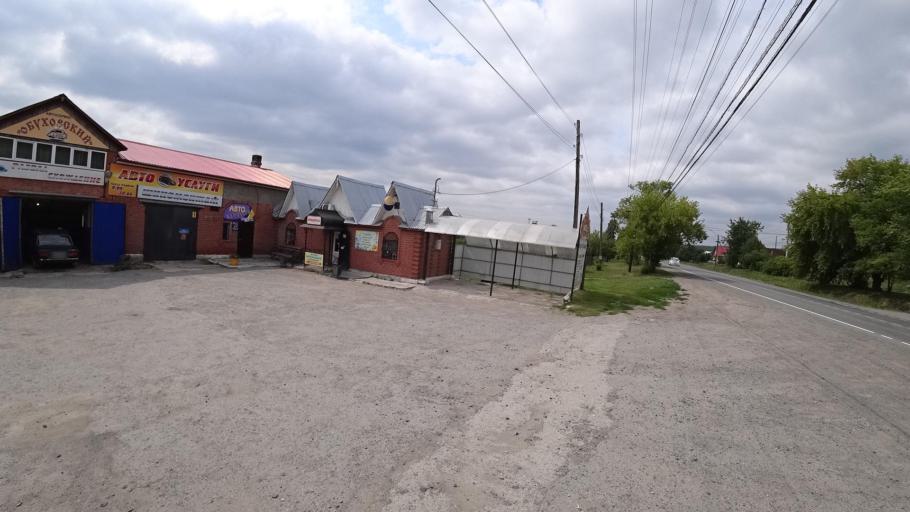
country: RU
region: Sverdlovsk
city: Obukhovskoye
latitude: 56.8439
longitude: 62.6440
